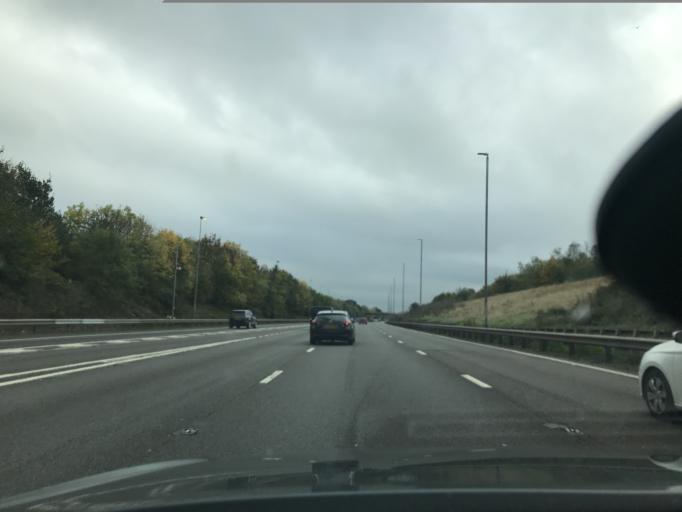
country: GB
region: England
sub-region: Solihull
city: Chelmsley Wood
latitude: 52.4936
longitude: -1.7146
